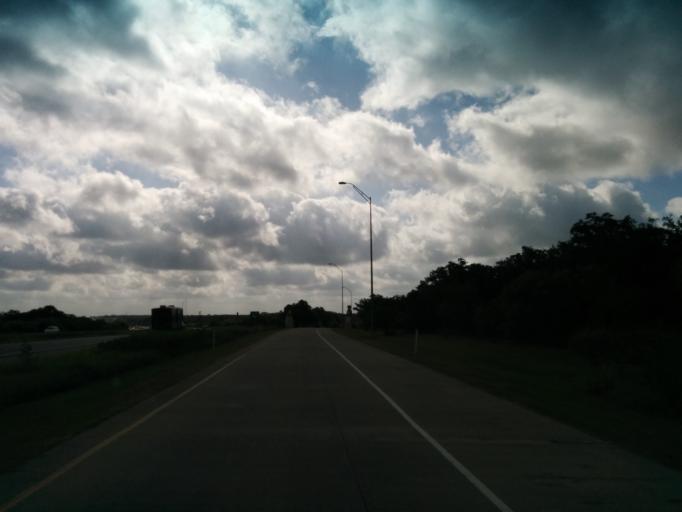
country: US
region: Texas
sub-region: Guadalupe County
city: Seguin
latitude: 29.6148
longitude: -97.8084
